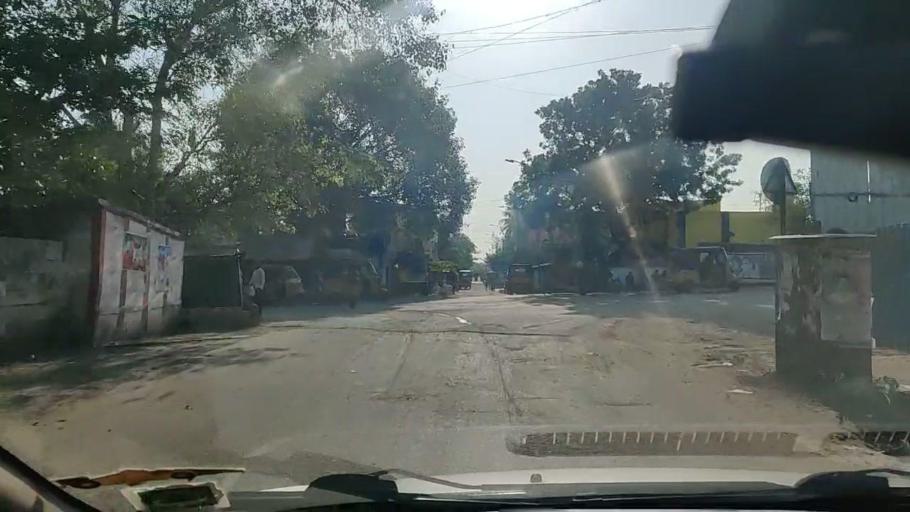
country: IN
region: Tamil Nadu
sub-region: Chennai
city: George Town
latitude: 13.1141
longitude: 80.2654
